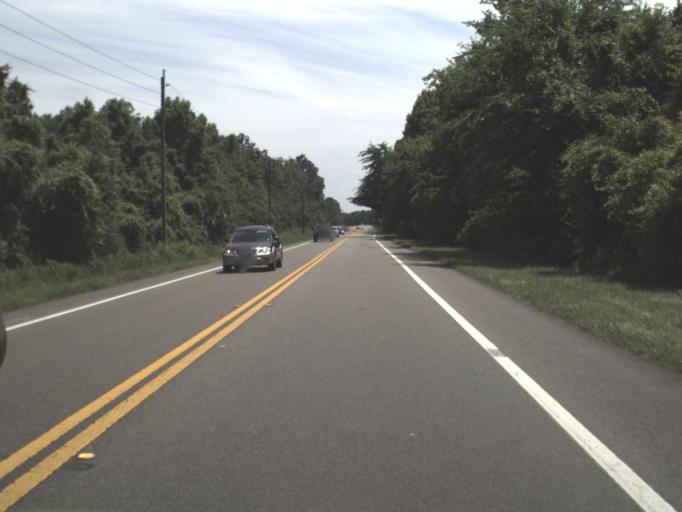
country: US
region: Florida
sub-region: Nassau County
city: Yulee
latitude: 30.5523
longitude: -81.6209
